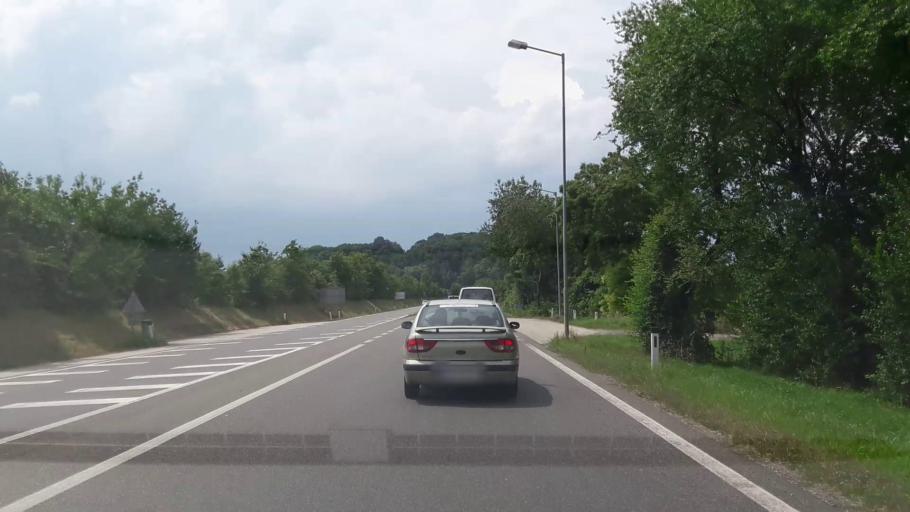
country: AT
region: Lower Austria
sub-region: Sankt Polten Stadt
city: Sankt Poelten
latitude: 48.1757
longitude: 15.6142
